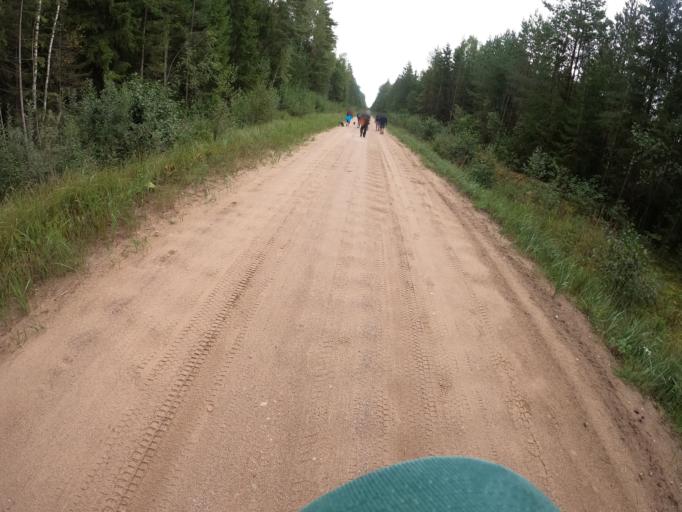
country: LV
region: Engure
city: Smarde
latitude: 56.9947
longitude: 23.3683
